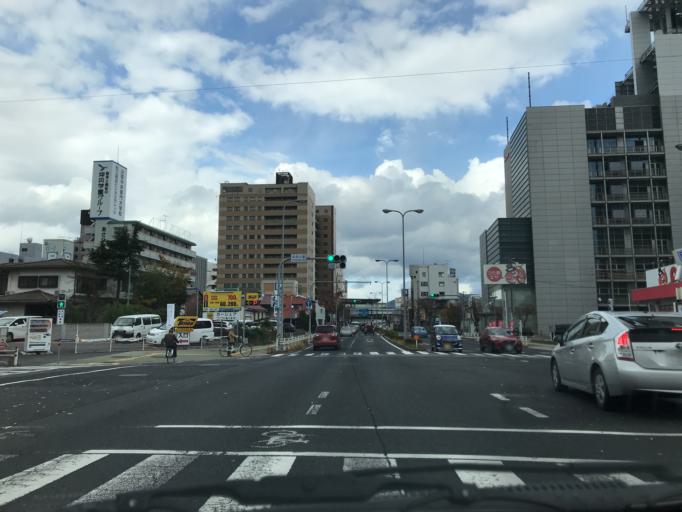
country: JP
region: Shimane
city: Matsue-shi
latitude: 35.4619
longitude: 133.0654
